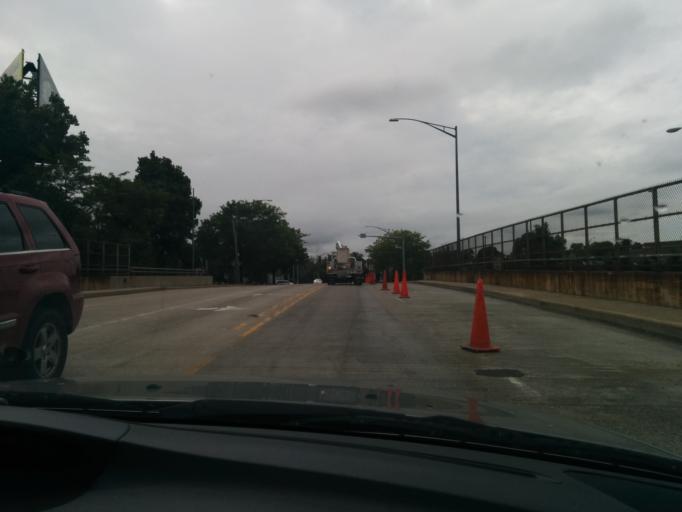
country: US
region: Illinois
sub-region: Cook County
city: Forest Park
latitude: 41.8735
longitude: -87.8155
